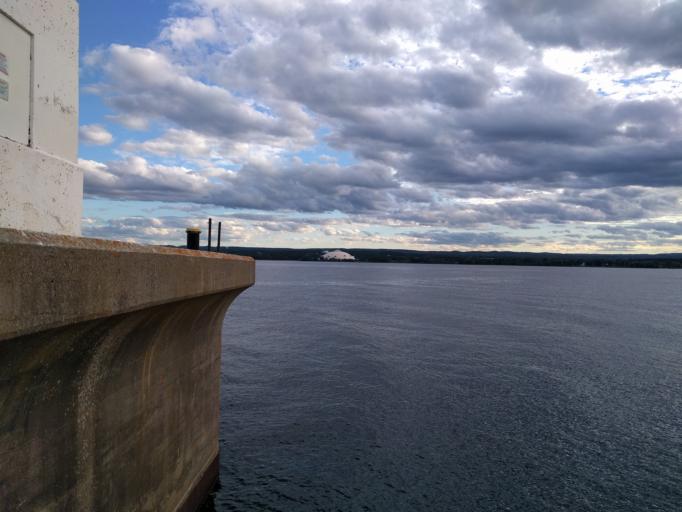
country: US
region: Michigan
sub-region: Marquette County
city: Marquette
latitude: 46.5743
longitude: -87.3746
